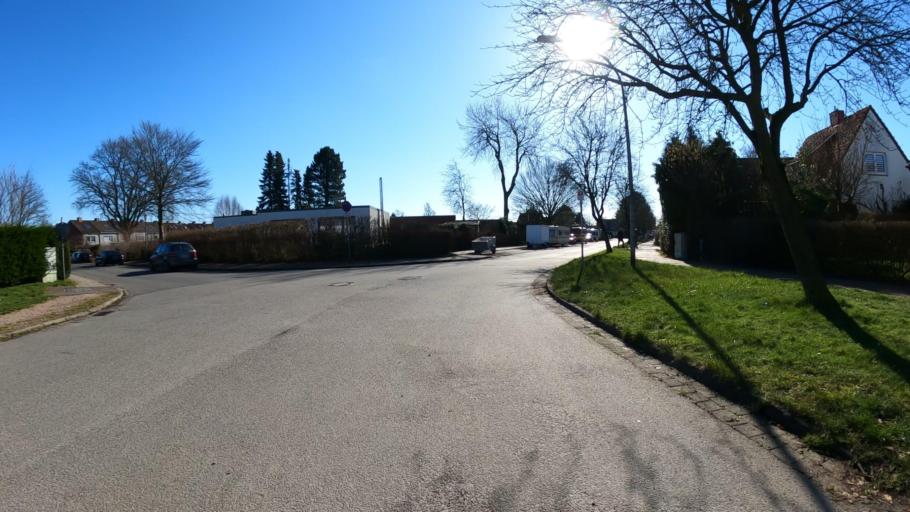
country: DE
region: Schleswig-Holstein
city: Pinneberg
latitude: 53.6760
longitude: 9.7888
